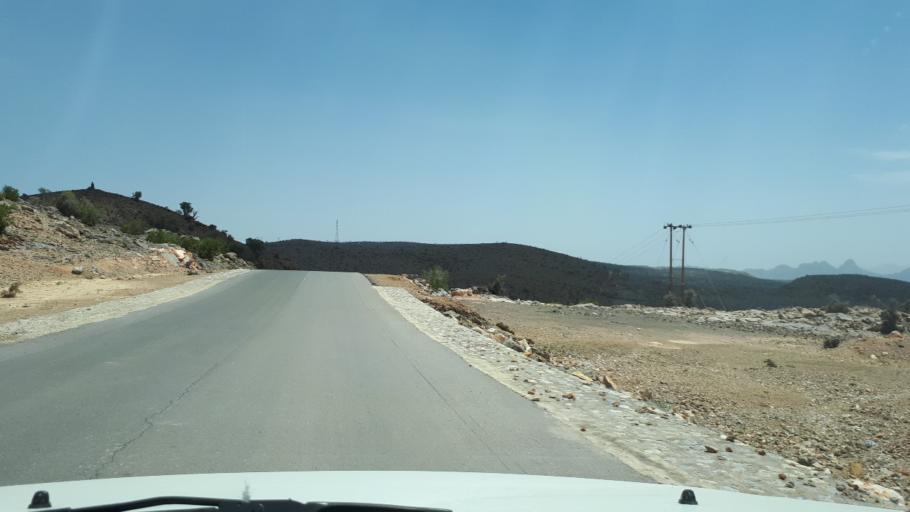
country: OM
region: Al Batinah
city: Rustaq
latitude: 23.2321
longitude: 57.1986
